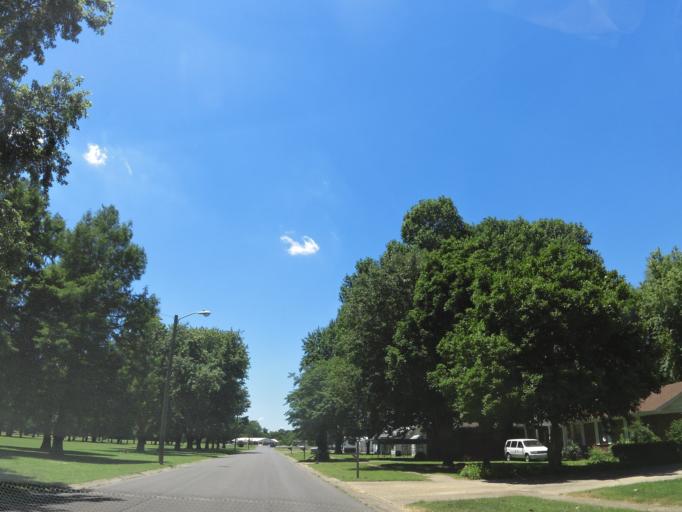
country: US
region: Missouri
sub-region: New Madrid County
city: New Madrid
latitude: 36.5861
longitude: -89.5434
